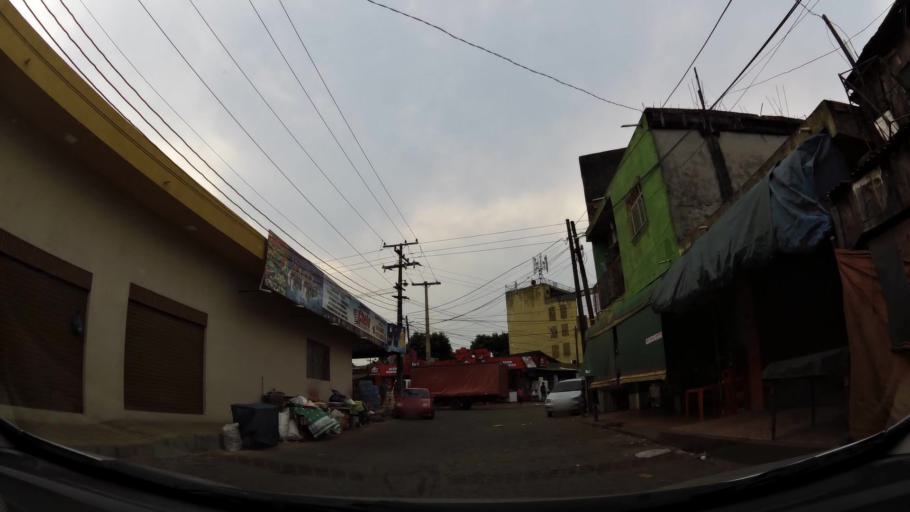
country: PY
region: Alto Parana
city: Presidente Franco
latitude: -25.5348
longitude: -54.6133
